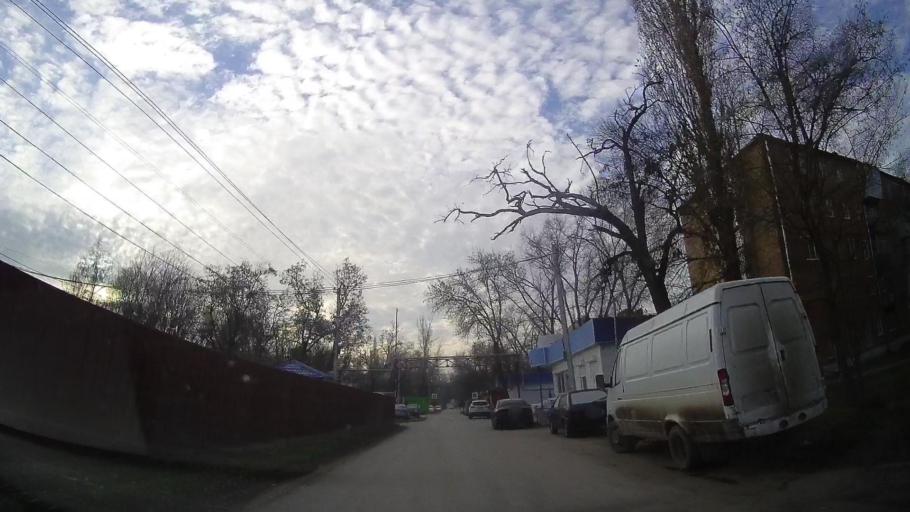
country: RU
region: Rostov
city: Bataysk
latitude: 47.1274
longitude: 39.7788
